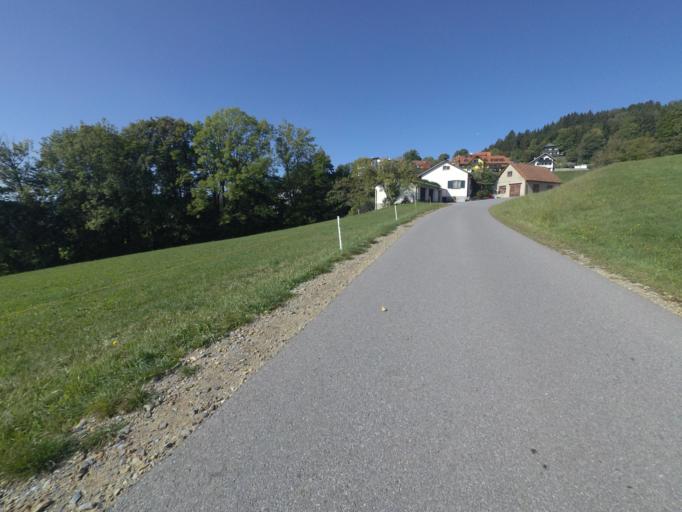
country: AT
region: Styria
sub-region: Politischer Bezirk Weiz
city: Passail
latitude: 47.2891
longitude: 15.4726
